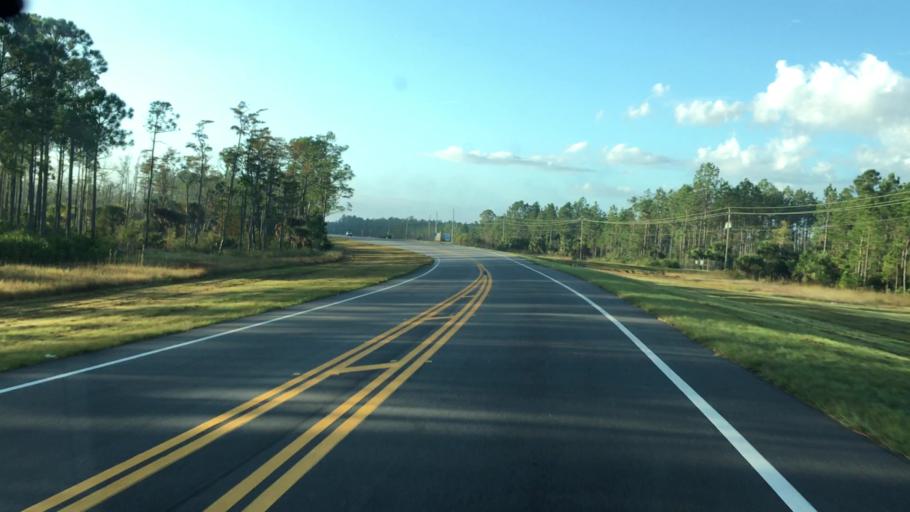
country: US
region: Florida
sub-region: Volusia County
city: Holly Hill
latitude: 29.2112
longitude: -81.1195
